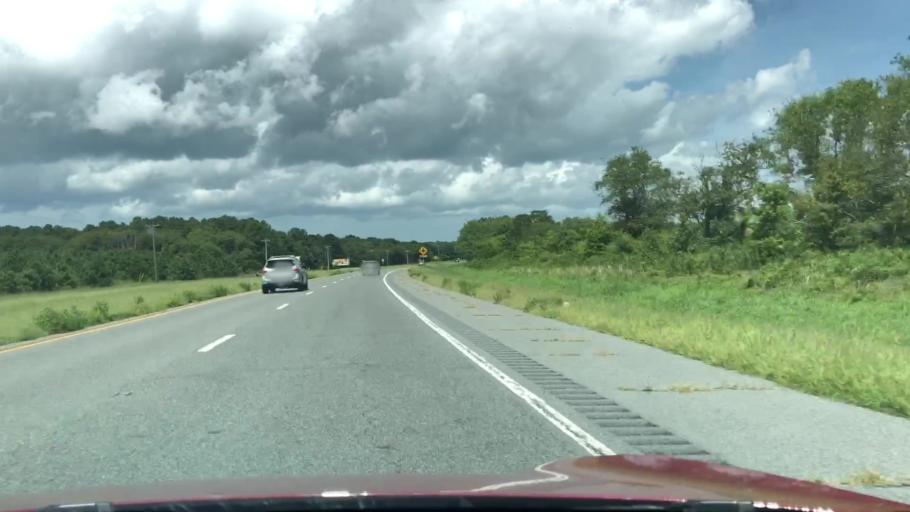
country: US
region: Virginia
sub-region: Northampton County
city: Cape Charles
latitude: 37.1449
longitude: -75.9700
